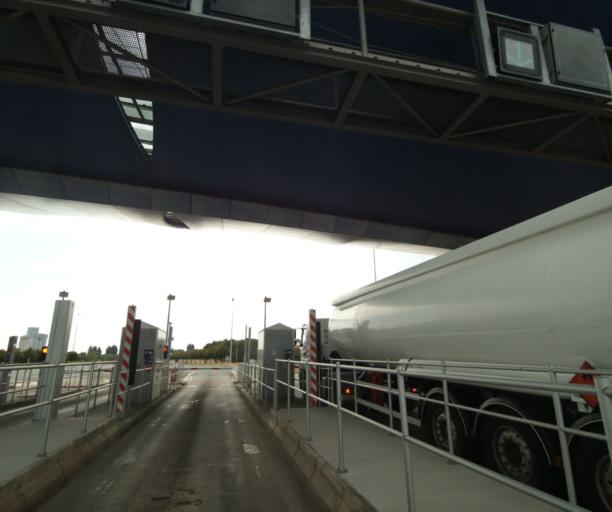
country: FR
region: Poitou-Charentes
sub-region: Departement de la Charente-Maritime
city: Tonnay-Charente
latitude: 45.9549
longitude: -0.8815
